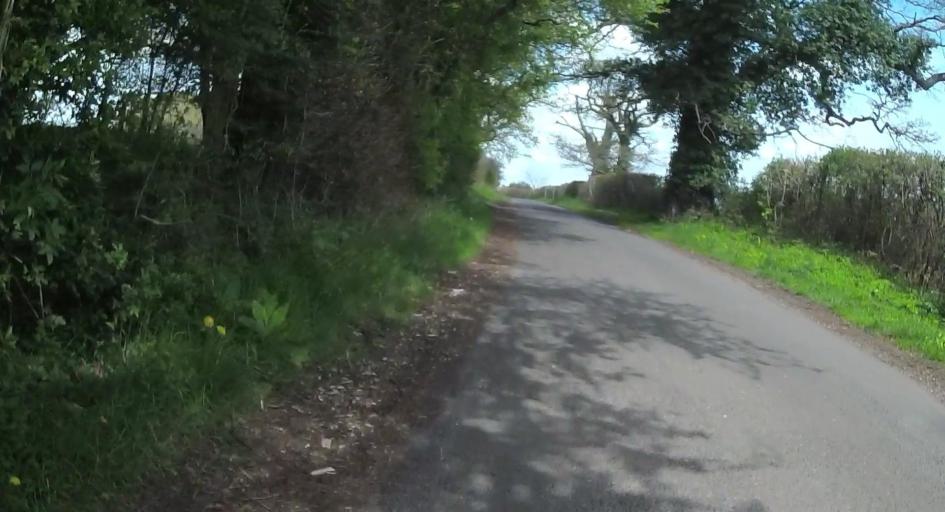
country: GB
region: England
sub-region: Hampshire
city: Romsey
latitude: 51.0495
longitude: -1.5362
